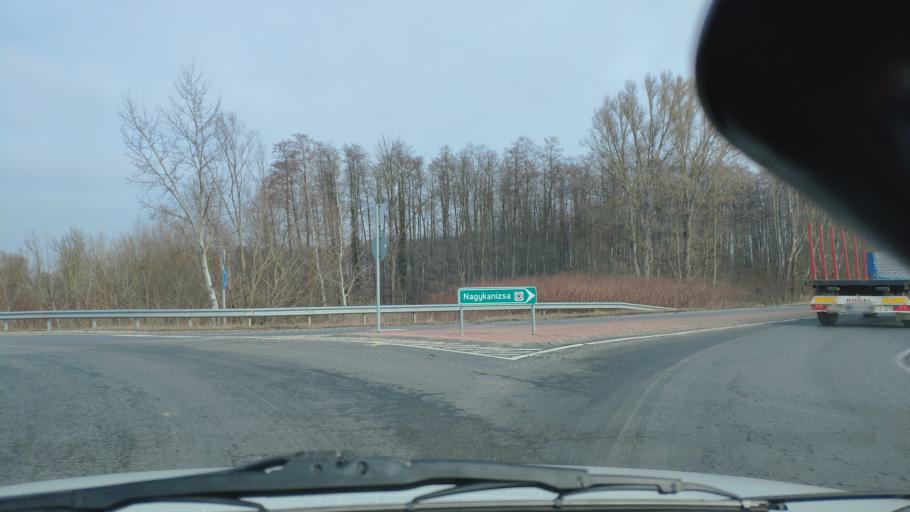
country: HU
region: Zala
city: Nagykanizsa
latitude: 46.4668
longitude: 16.9695
